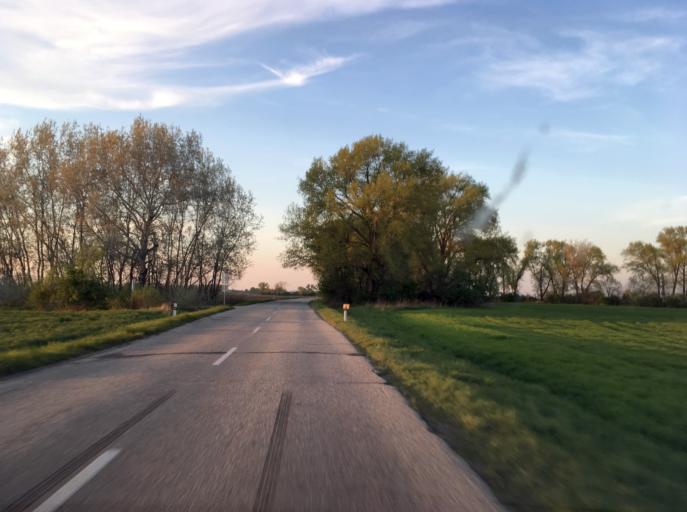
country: SK
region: Nitriansky
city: Kolarovo
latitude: 47.8965
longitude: 17.9243
